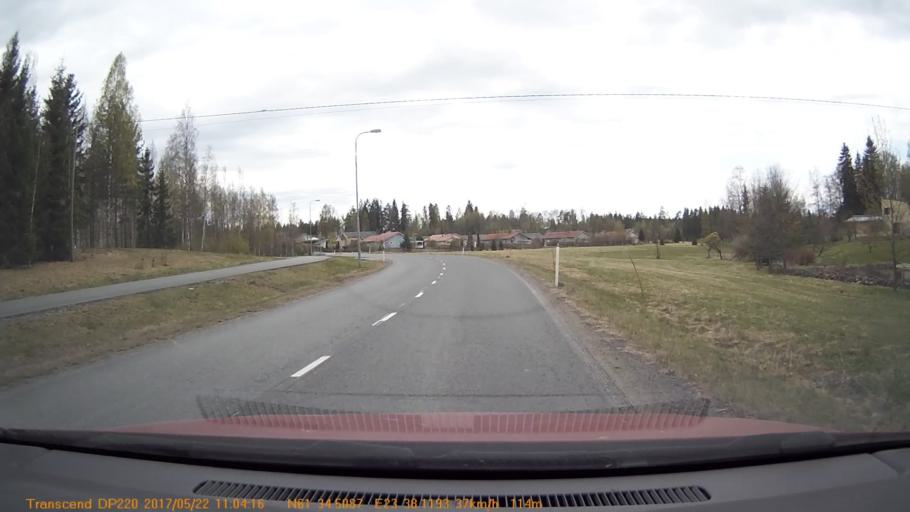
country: FI
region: Pirkanmaa
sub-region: Tampere
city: Yloejaervi
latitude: 61.5752
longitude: 23.6354
